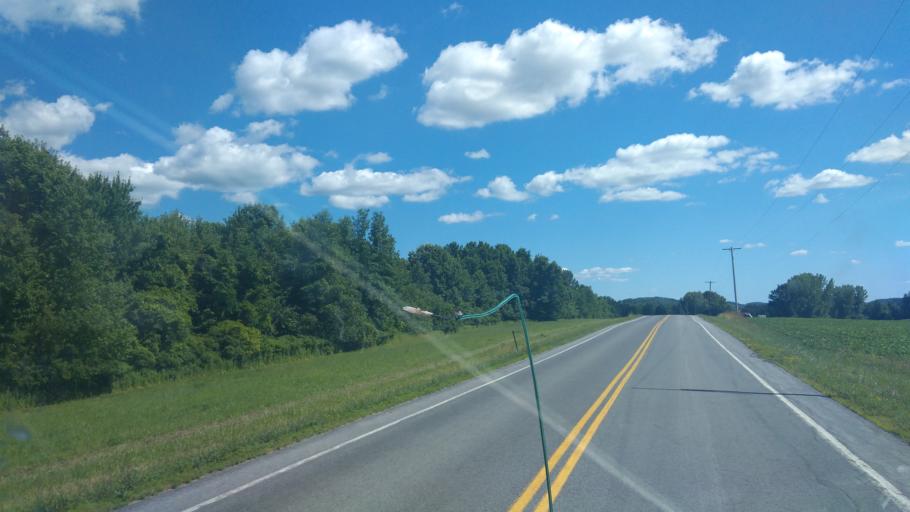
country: US
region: New York
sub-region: Wayne County
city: Lyons
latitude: 43.1470
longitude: -77.0148
